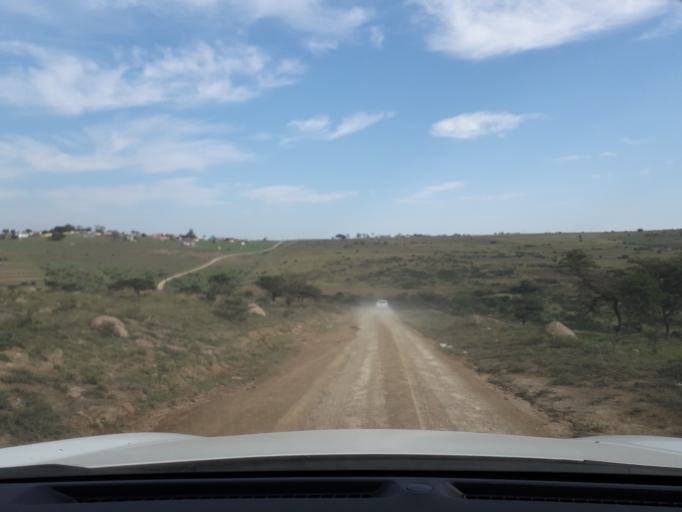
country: ZA
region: Eastern Cape
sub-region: Buffalo City Metropolitan Municipality
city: Bhisho
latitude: -32.9946
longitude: 27.3408
